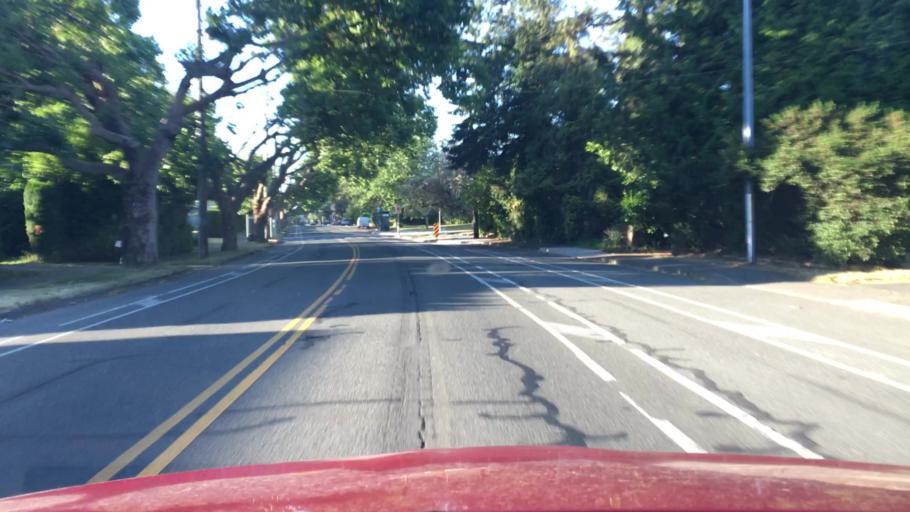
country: CA
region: British Columbia
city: Oak Bay
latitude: 48.4806
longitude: -123.3361
